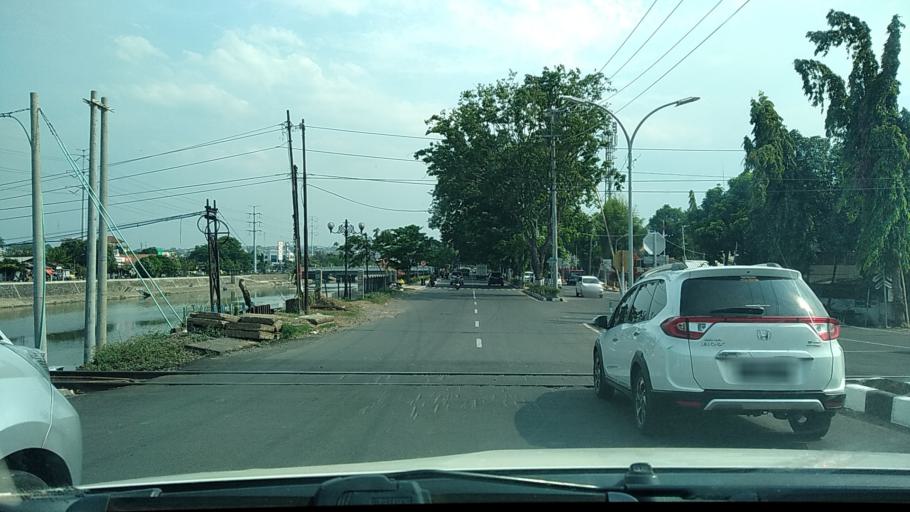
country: ID
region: Central Java
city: Semarang
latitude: -6.9774
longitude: 110.4010
